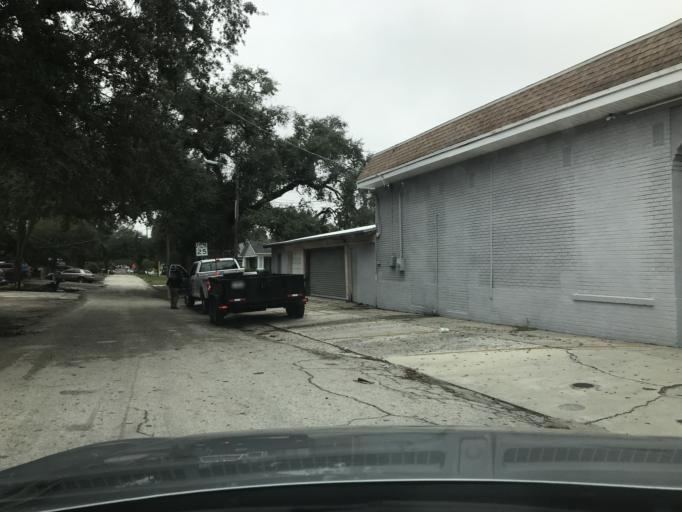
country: US
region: Florida
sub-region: Hillsborough County
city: Tampa
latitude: 27.9881
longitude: -82.4595
